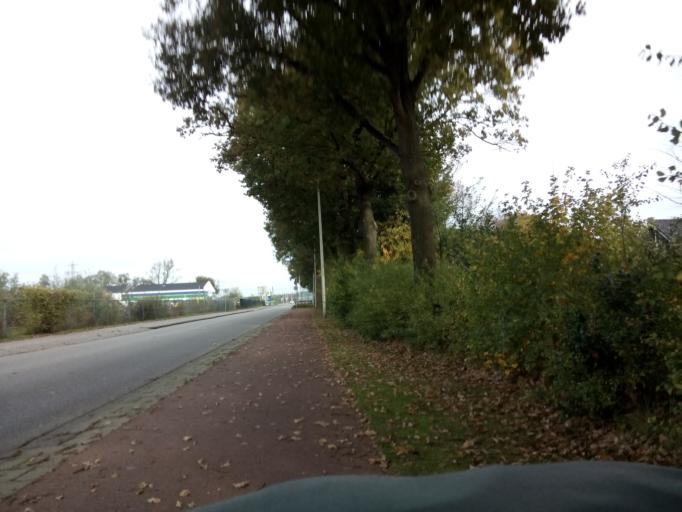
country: NL
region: Drenthe
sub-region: Gemeente Hoogeveen
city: Hoogeveen
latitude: 52.7277
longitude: 6.4679
